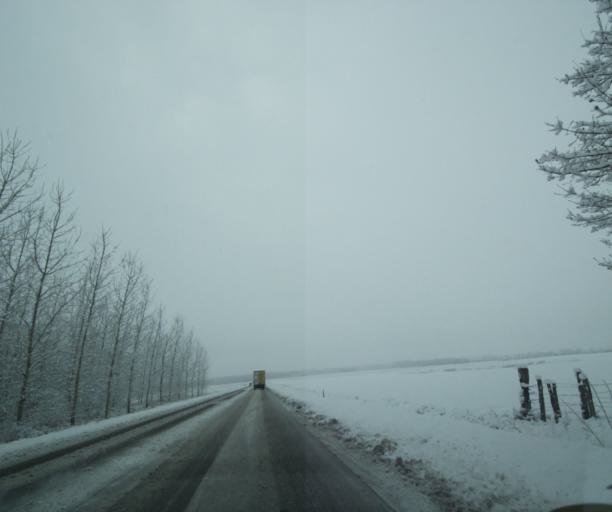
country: FR
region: Champagne-Ardenne
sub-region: Departement de la Haute-Marne
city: Saint-Dizier
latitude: 48.5987
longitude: 4.8958
